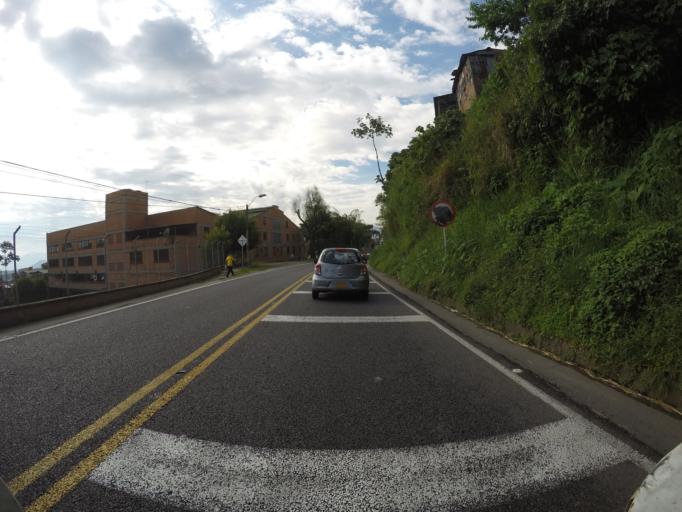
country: CO
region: Risaralda
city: Pereira
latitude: 4.7974
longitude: -75.6947
